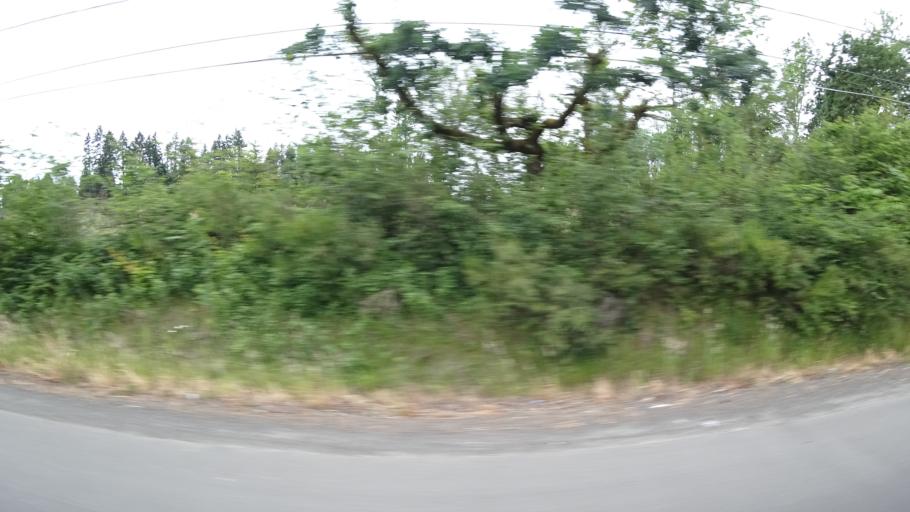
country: US
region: Oregon
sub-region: Washington County
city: Hillsboro
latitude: 45.4844
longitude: -122.9362
